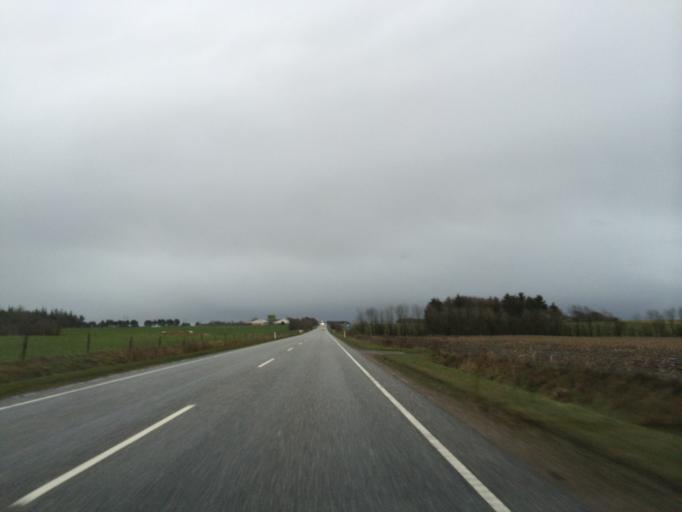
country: DK
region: South Denmark
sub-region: Varde Kommune
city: Varde
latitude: 55.7615
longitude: 8.4930
